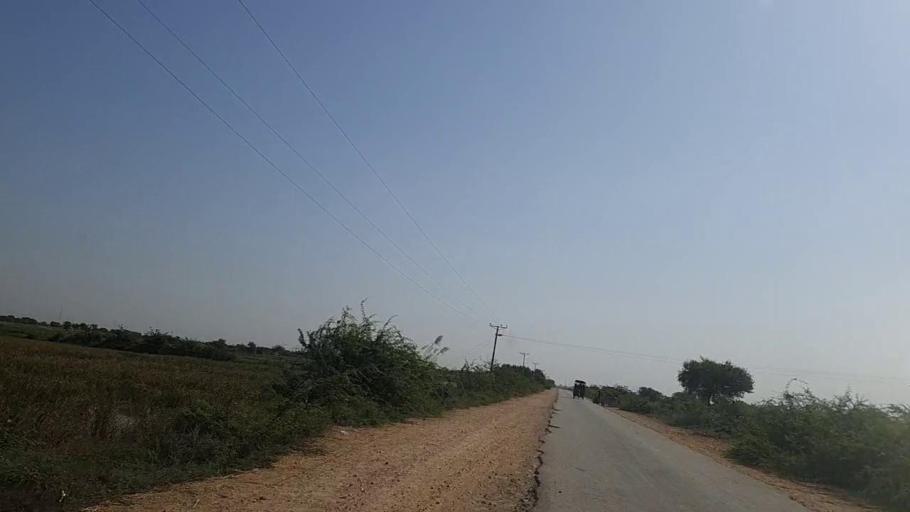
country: PK
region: Sindh
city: Mirpur Batoro
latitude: 24.6370
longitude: 68.2917
